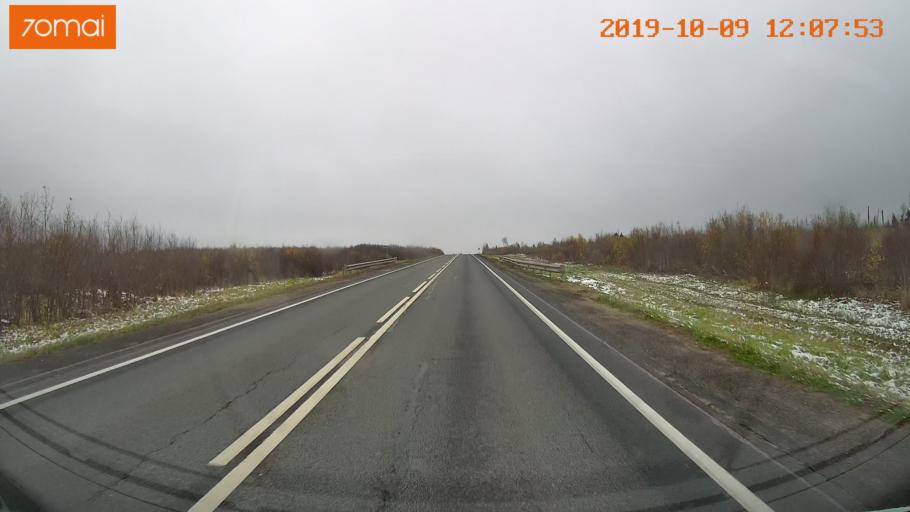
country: RU
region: Jaroslavl
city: Prechistoye
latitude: 58.5939
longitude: 40.3444
